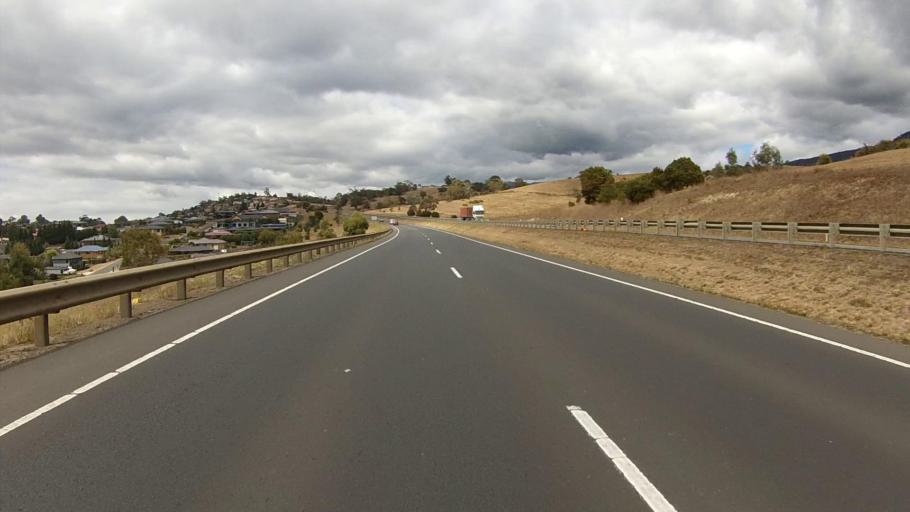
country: AU
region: Tasmania
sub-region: Glenorchy
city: Austins Ferry
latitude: -42.7649
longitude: 147.2354
